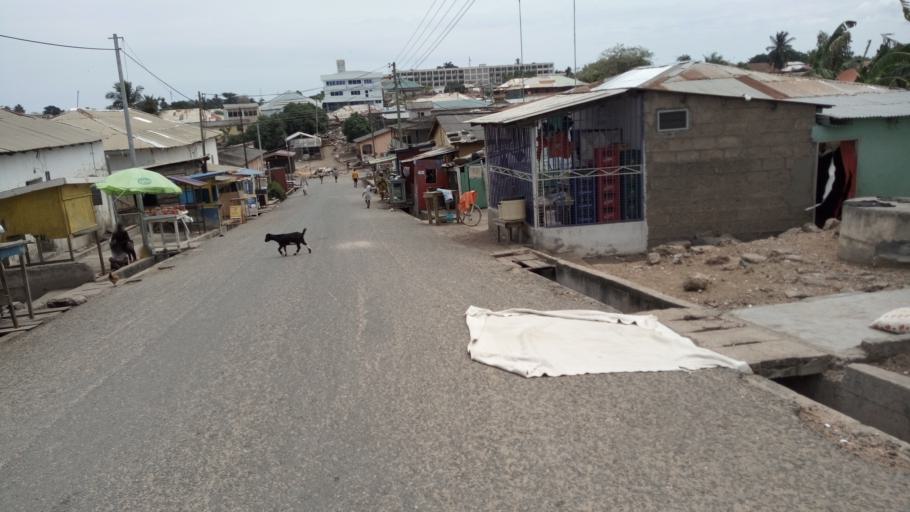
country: GH
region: Central
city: Winneba
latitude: 5.3421
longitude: -0.6223
